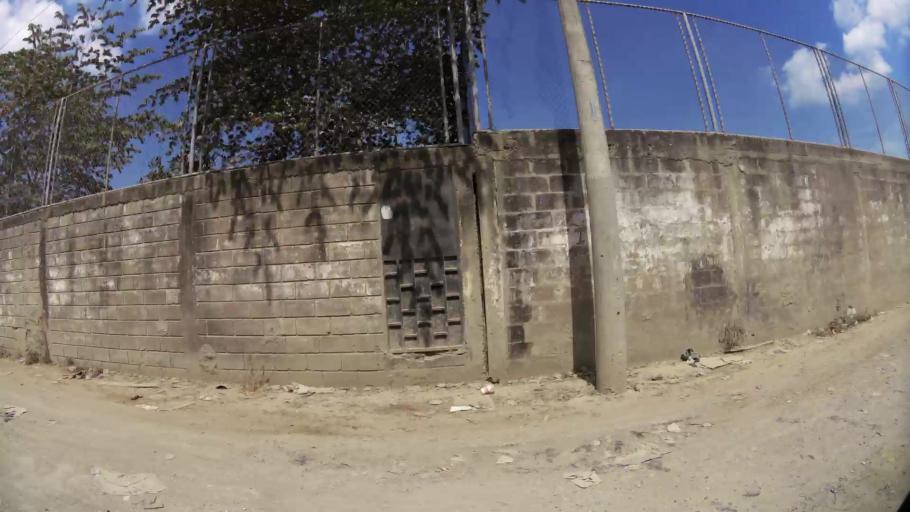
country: EC
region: Guayas
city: Guayaquil
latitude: -2.1263
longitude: -79.9295
